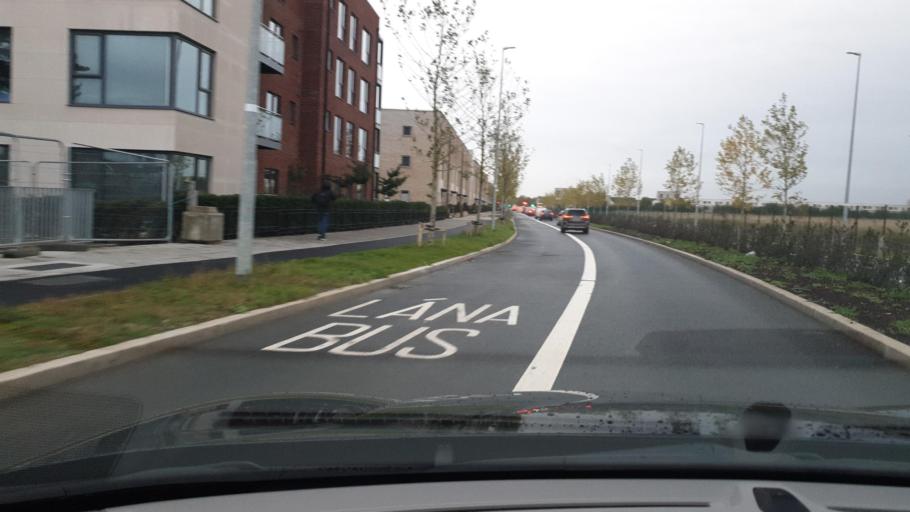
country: IE
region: Leinster
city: Lucan
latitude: 53.3437
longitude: -6.4670
